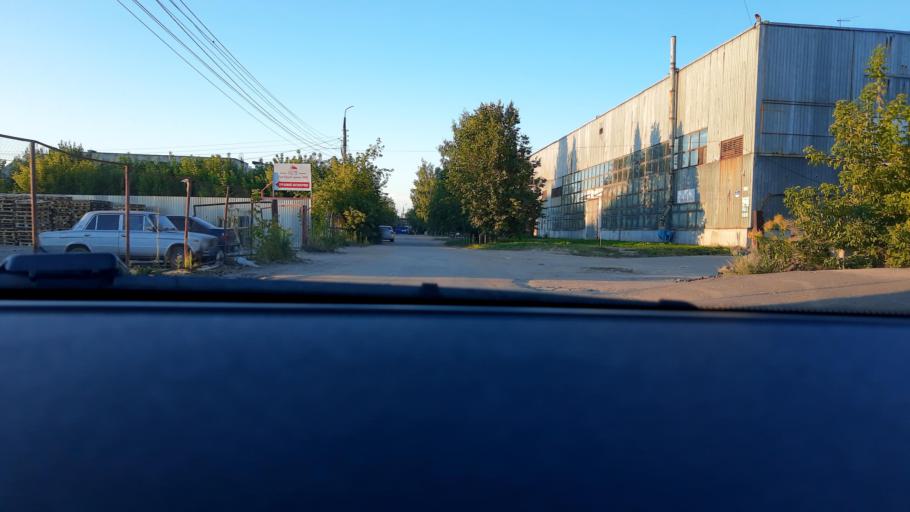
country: RU
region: Nizjnij Novgorod
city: Gorbatovka
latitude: 56.3175
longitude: 43.8568
